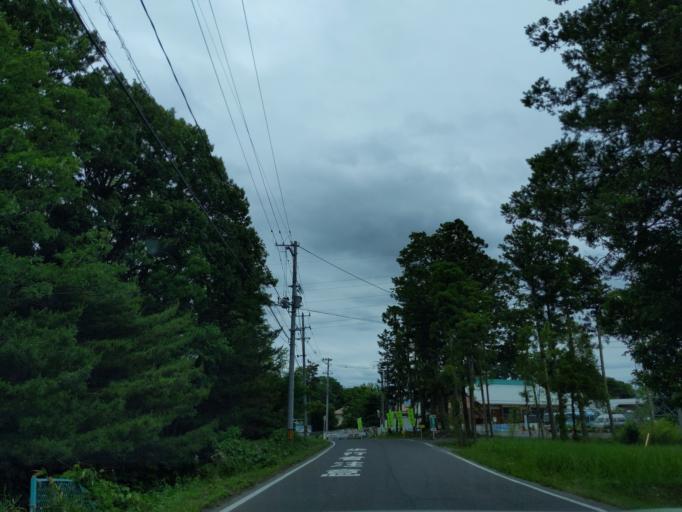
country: JP
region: Fukushima
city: Koriyama
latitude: 37.3451
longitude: 140.3422
